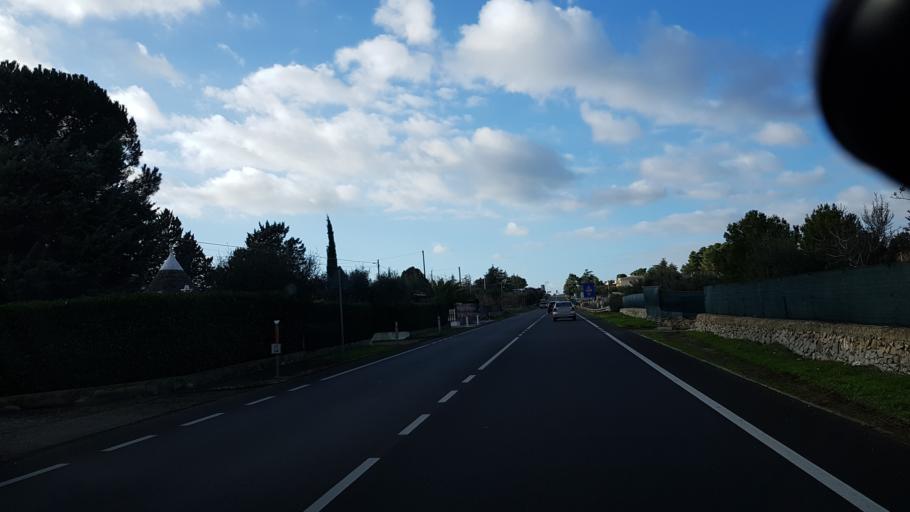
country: IT
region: Apulia
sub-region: Provincia di Bari
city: Putignano
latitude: 40.8380
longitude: 17.1549
